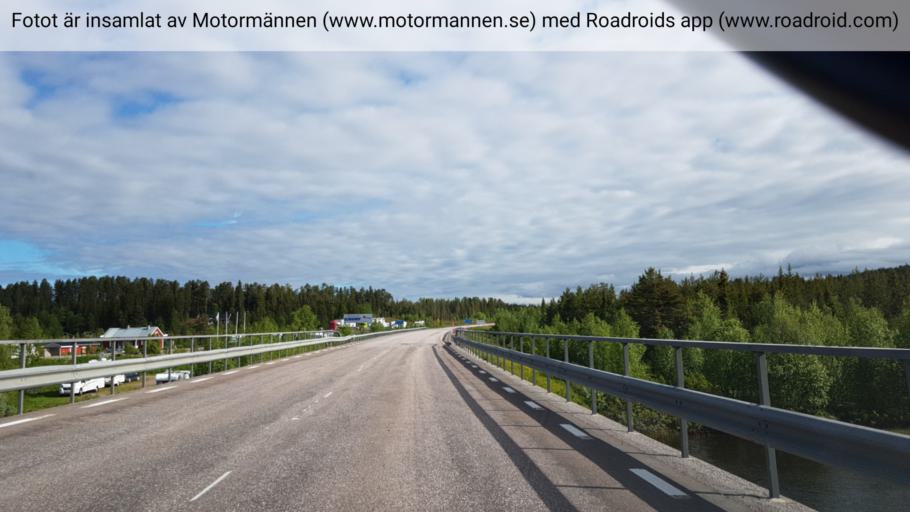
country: SE
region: Norrbotten
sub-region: Gallivare Kommun
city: Malmberget
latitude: 67.4888
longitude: 21.1207
